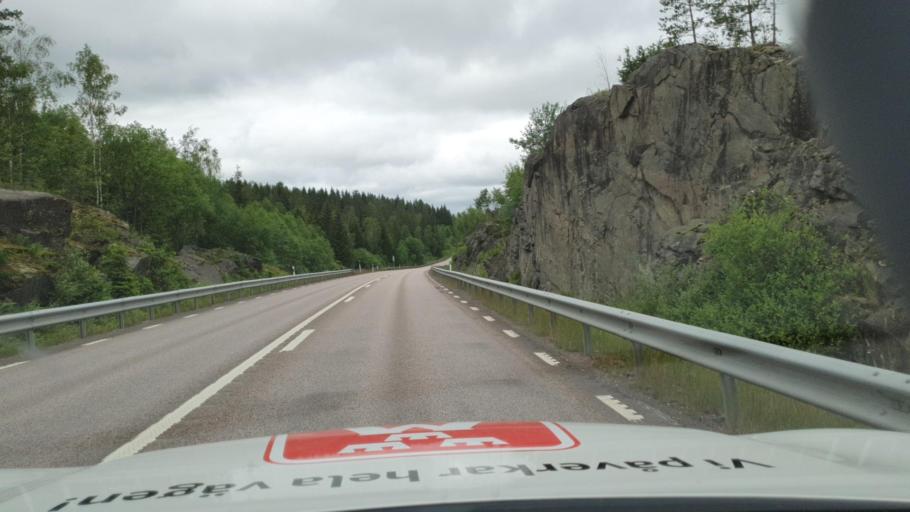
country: SE
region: Vaermland
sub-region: Karlstads Kommun
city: Edsvalla
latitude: 59.5449
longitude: 13.0696
